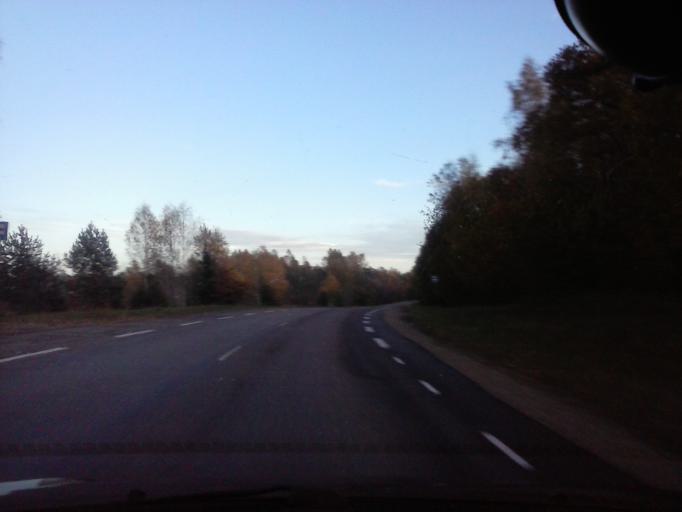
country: EE
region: Harju
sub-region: Nissi vald
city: Turba
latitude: 58.9161
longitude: 24.1950
